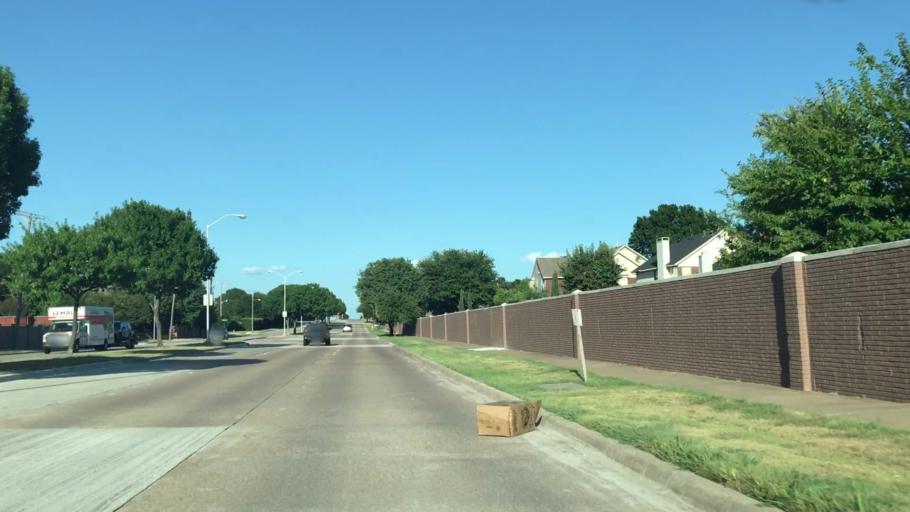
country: US
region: Texas
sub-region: Collin County
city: Plano
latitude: 33.0714
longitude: -96.7314
